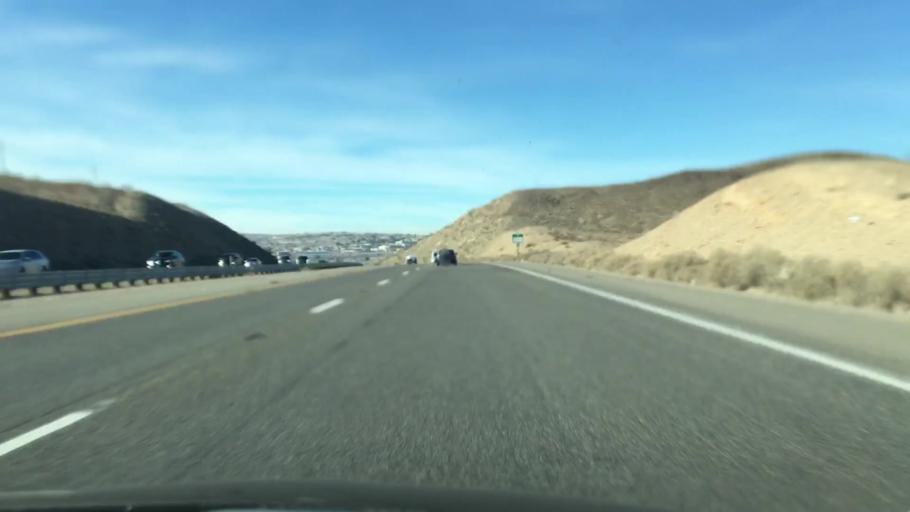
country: US
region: California
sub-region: San Bernardino County
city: Barstow
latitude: 34.9060
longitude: -116.9792
